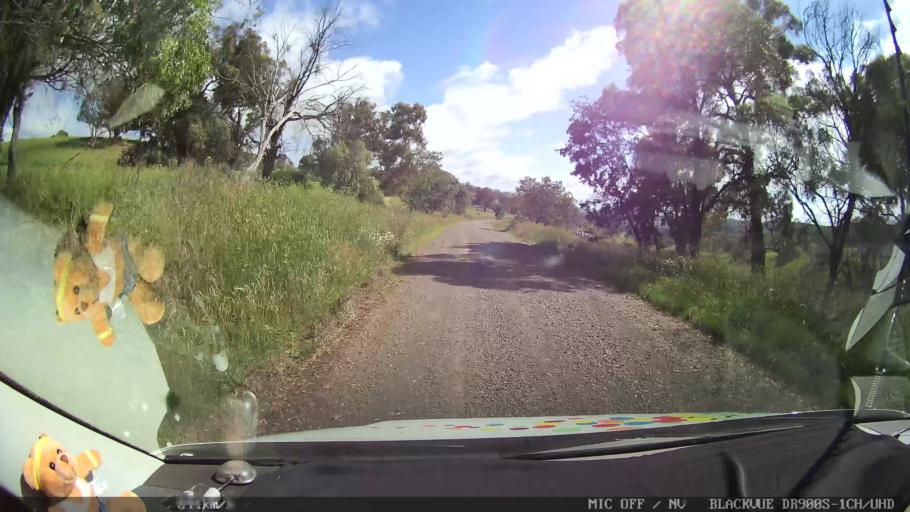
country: AU
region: New South Wales
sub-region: Guyra
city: Guyra
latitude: -30.0040
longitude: 151.6690
